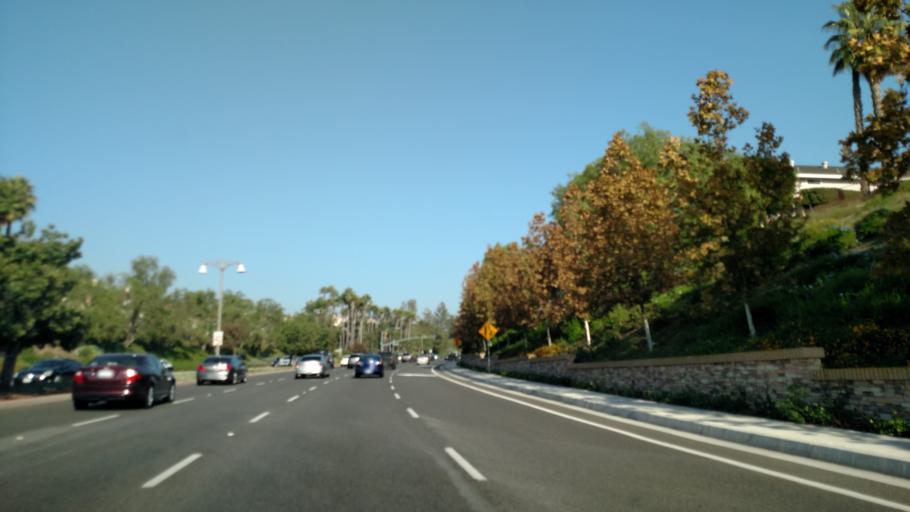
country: US
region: California
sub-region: Orange County
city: Mission Viejo
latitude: 33.5852
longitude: -117.6573
